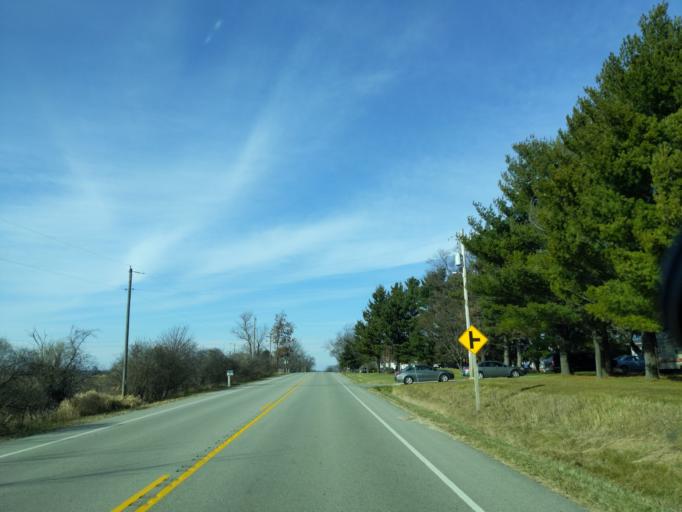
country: US
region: Wisconsin
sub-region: Walworth County
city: Elkhorn
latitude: 42.6902
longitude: -88.5590
